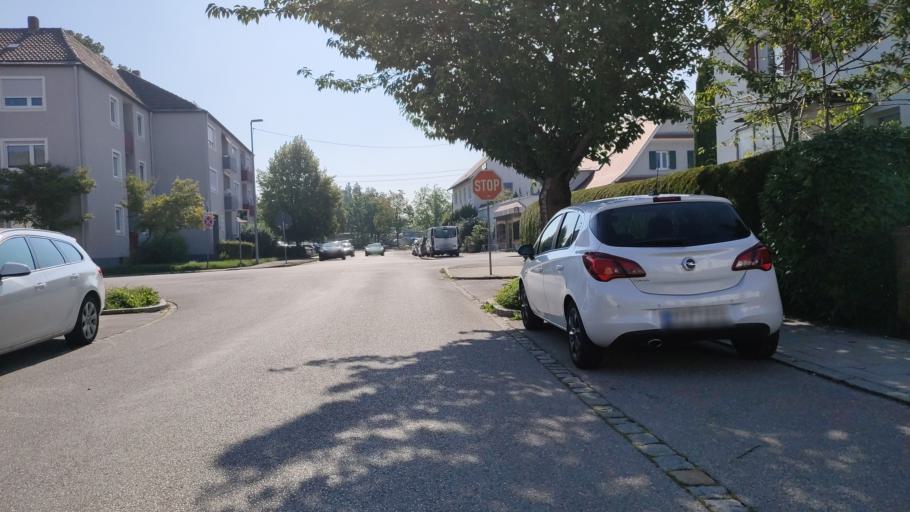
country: DE
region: Bavaria
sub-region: Swabia
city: Bobingen
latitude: 48.2678
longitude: 10.8365
